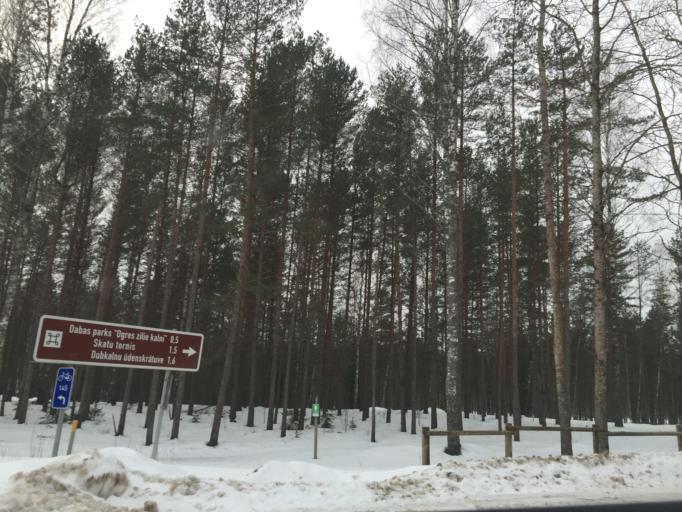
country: LV
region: Ogre
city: Ogre
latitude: 56.8376
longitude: 24.5777
